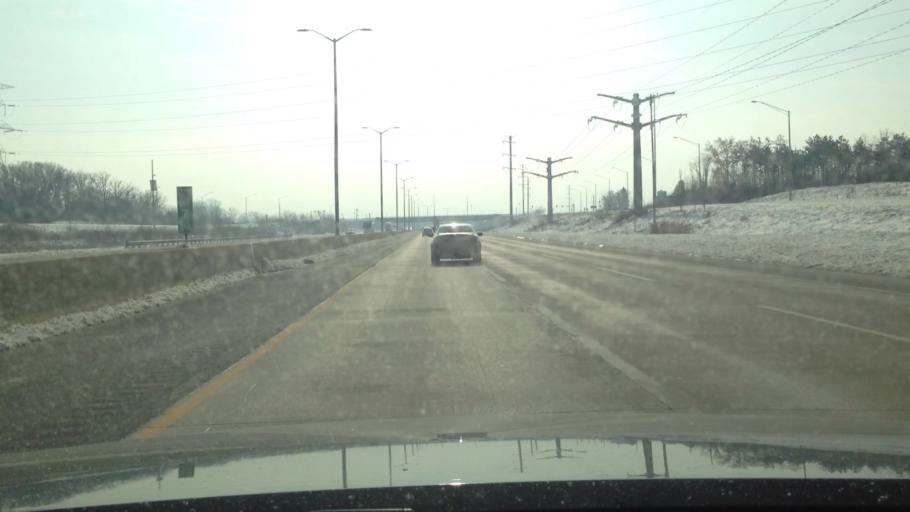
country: US
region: Illinois
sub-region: Cook County
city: Lemont
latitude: 41.6330
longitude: -88.0116
